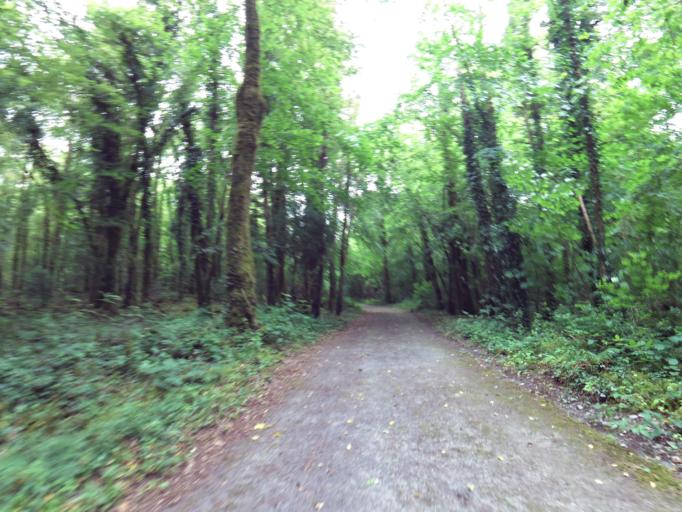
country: IE
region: Connaught
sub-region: County Galway
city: Gort
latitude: 53.0771
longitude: -8.8712
